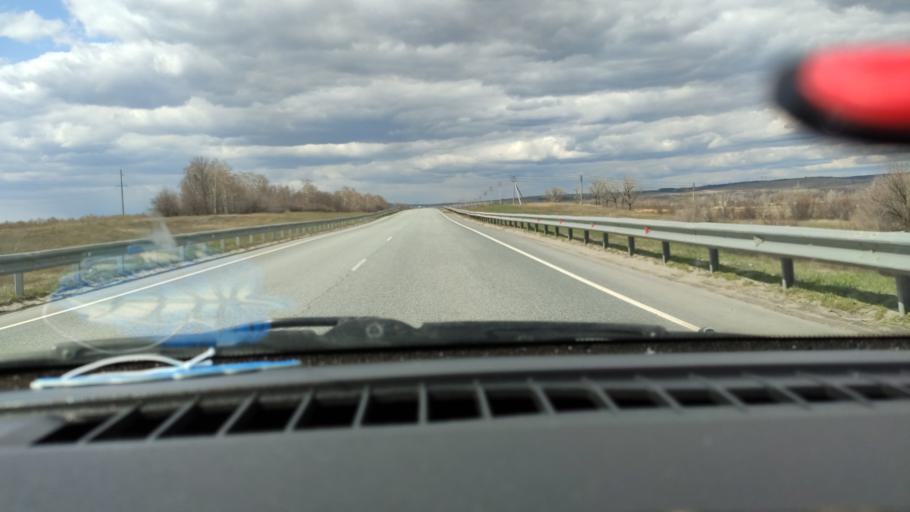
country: RU
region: Saratov
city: Tersa
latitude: 52.0850
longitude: 47.6349
